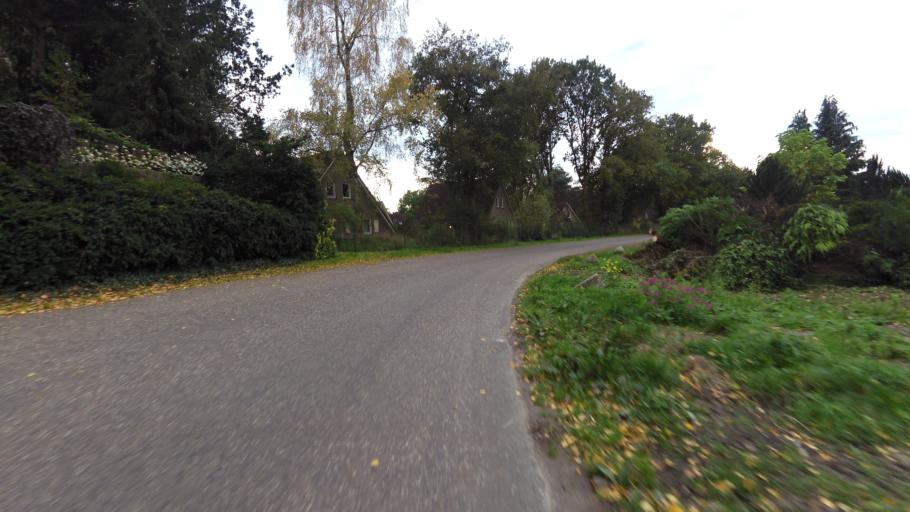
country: NL
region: Gelderland
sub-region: Gemeente Oldebroek
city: Oldebroek
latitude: 52.4406
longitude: 5.9487
